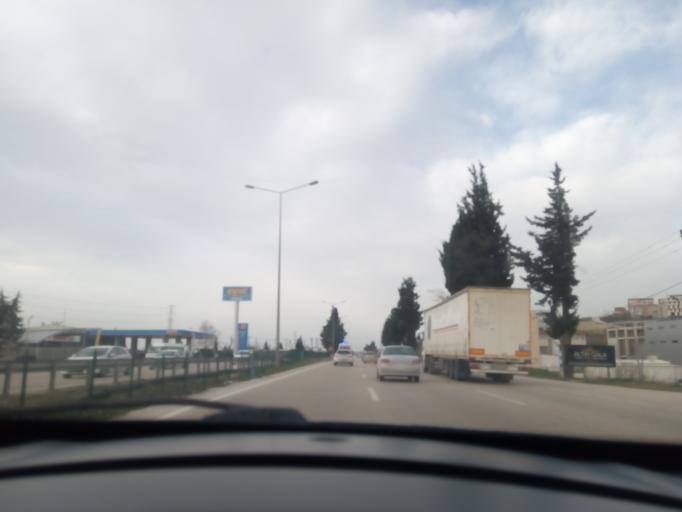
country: TR
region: Bursa
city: Gorukle
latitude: 40.2170
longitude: 28.8459
